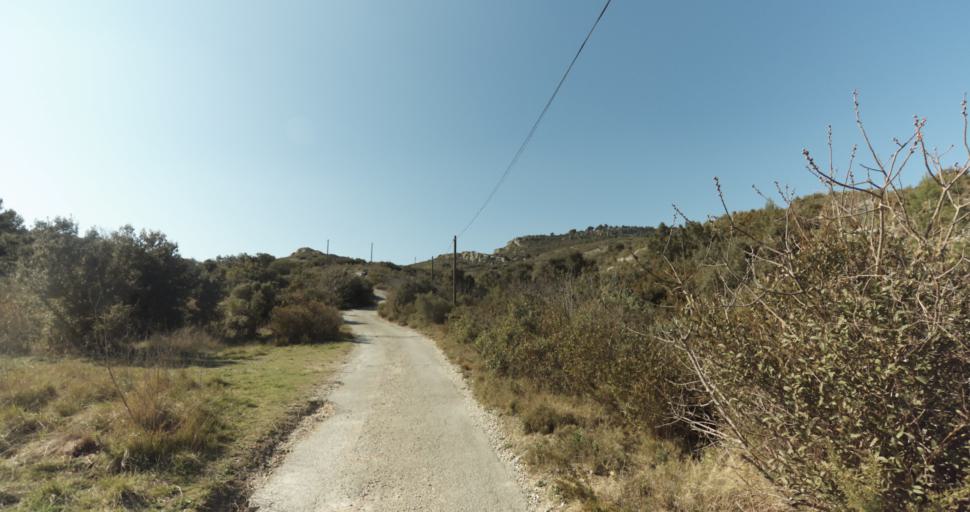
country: FR
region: Provence-Alpes-Cote d'Azur
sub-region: Departement des Bouches-du-Rhone
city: Pelissanne
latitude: 43.6460
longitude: 5.1423
